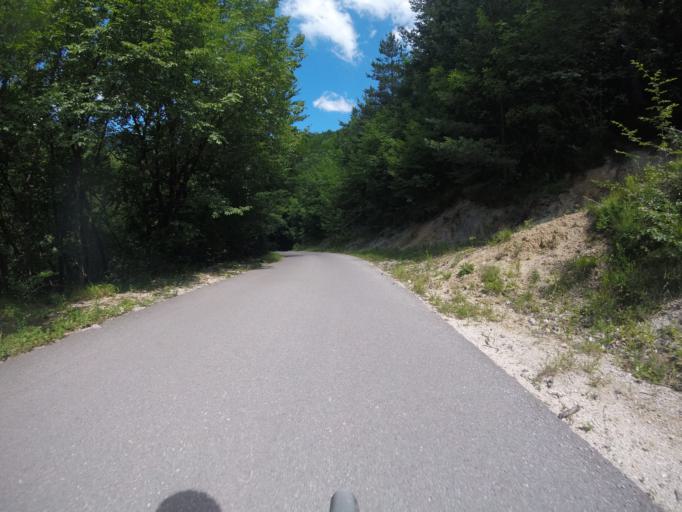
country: SI
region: Kostanjevica na Krki
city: Kostanjevica na Krki
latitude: 45.7652
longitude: 15.4075
